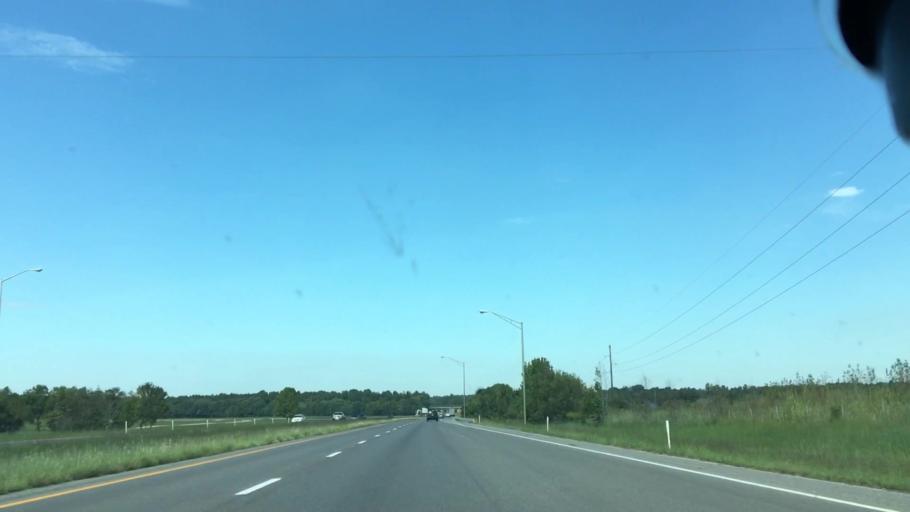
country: US
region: Kentucky
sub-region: Hopkins County
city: Madisonville
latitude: 37.2990
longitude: -87.4638
